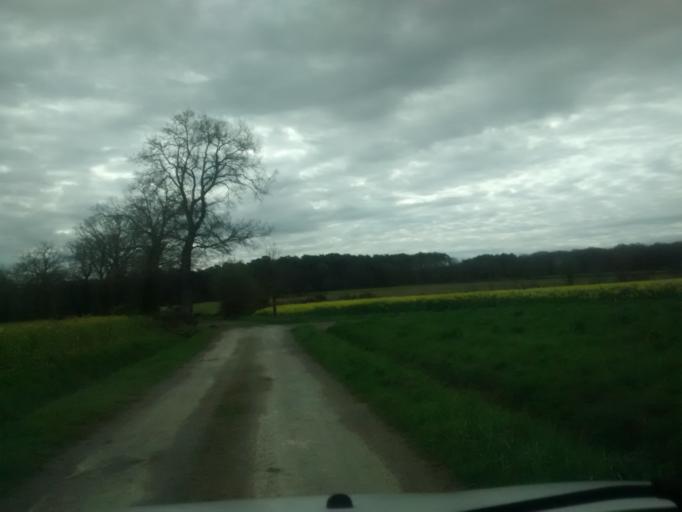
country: FR
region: Brittany
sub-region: Departement d'Ille-et-Vilaine
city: Chasne-sur-Illet
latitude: 48.2241
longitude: -1.5606
